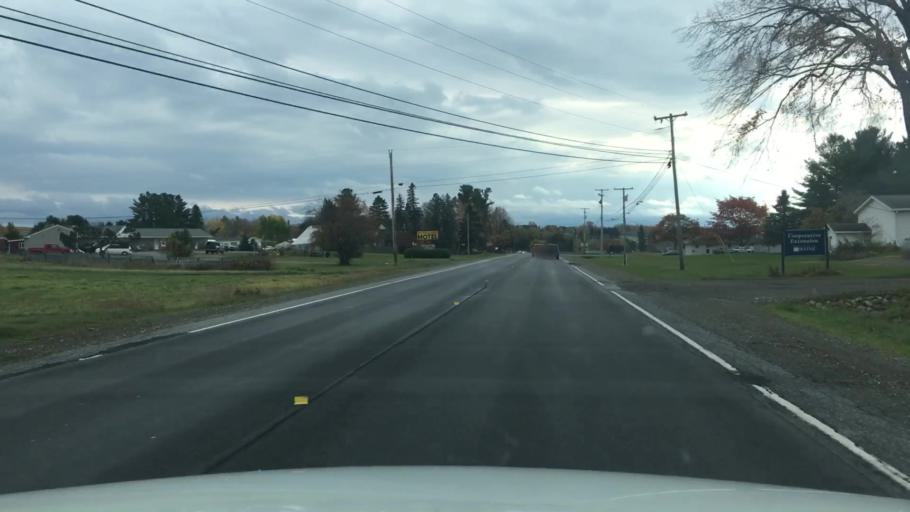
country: US
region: Maine
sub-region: Aroostook County
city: Presque Isle
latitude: 46.6558
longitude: -68.0058
